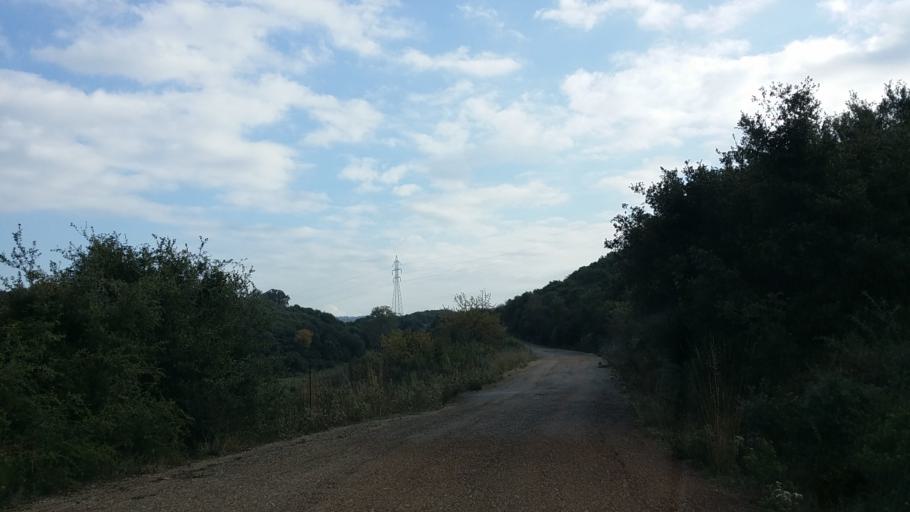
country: GR
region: West Greece
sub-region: Nomos Aitolias kai Akarnanias
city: Katouna
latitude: 38.8596
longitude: 21.0575
